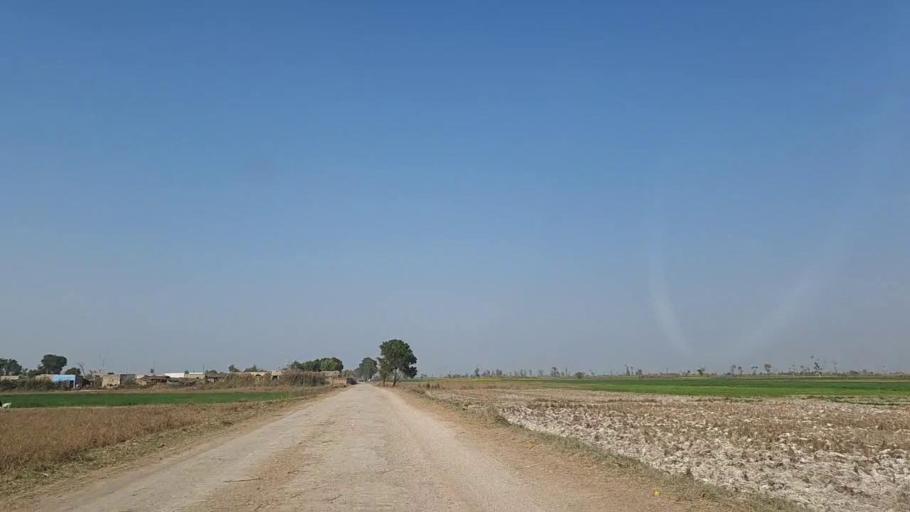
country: PK
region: Sindh
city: Daur
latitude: 26.4766
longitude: 68.2971
